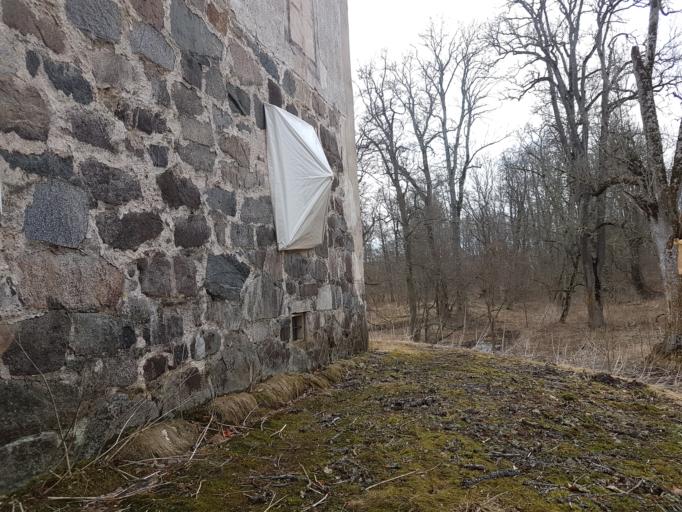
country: SE
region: Stockholm
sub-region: Norrtalje Kommun
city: Norrtalje
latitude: 59.6817
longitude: 18.6728
